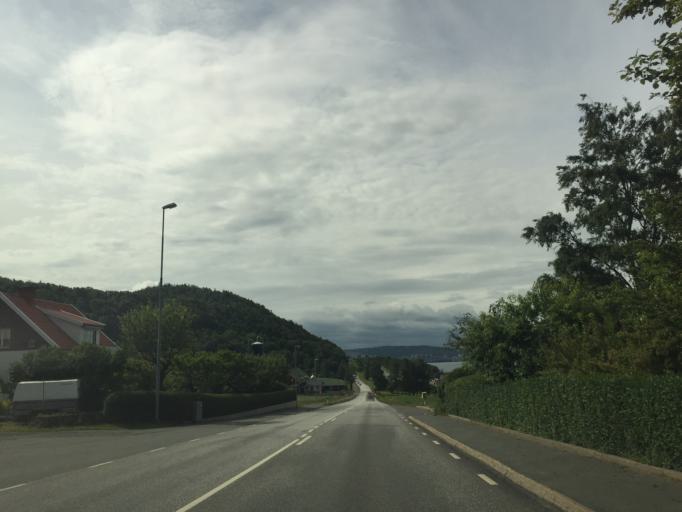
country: SE
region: Joenkoeping
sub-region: Jonkopings Kommun
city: Kaxholmen
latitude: 57.8367
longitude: 14.2727
